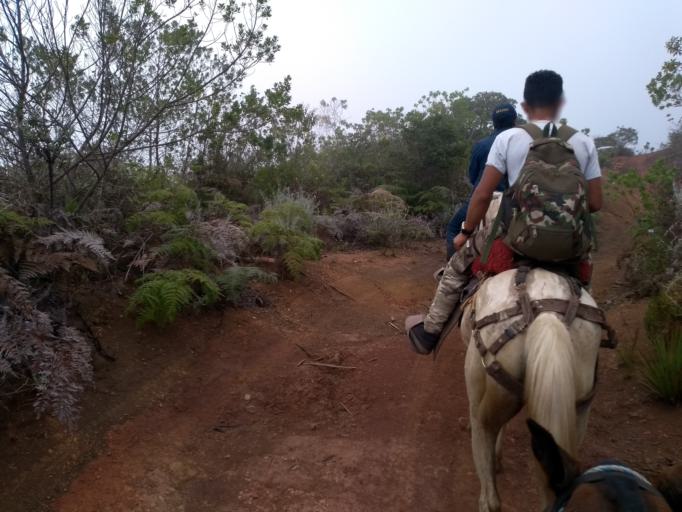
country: CO
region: Cesar
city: San Diego
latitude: 10.1800
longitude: -73.0423
